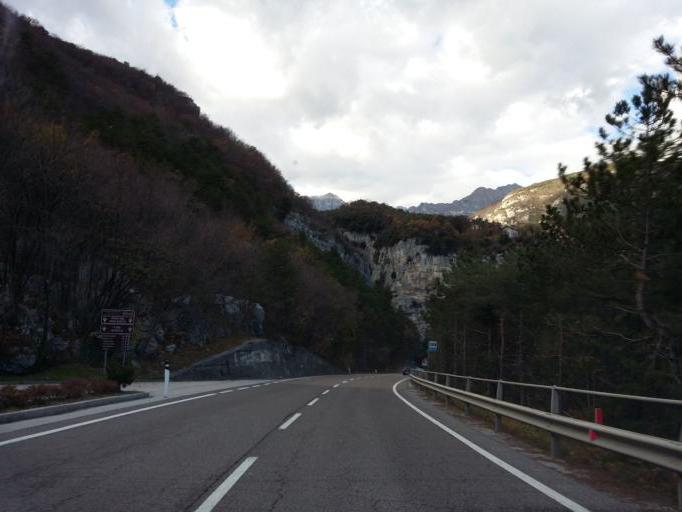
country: IT
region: Trentino-Alto Adige
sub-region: Provincia di Trento
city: Pietramurata
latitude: 46.0445
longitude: 10.9429
